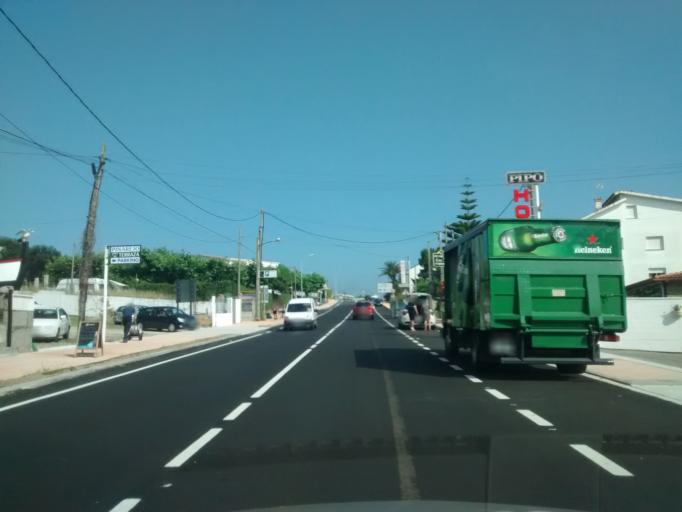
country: ES
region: Galicia
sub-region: Provincia de Pontevedra
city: Sanxenxo
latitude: 42.4205
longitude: -8.8722
